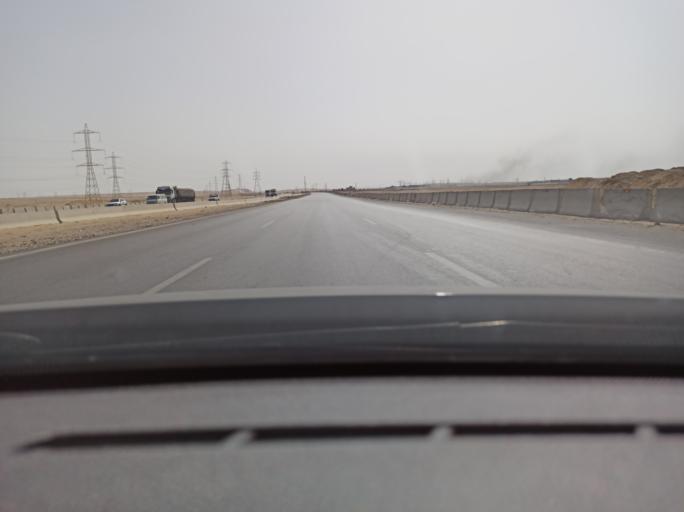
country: EG
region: Muhafazat al Qahirah
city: Halwan
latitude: 29.7696
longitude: 31.3793
